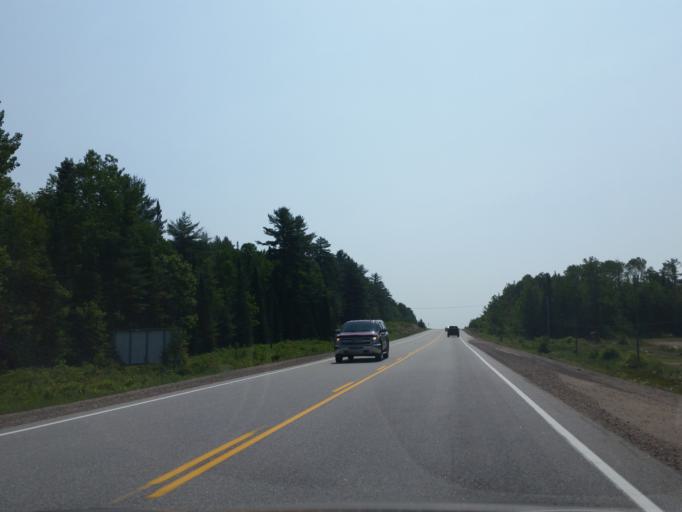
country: CA
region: Ontario
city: Mattawa
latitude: 46.3013
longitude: -78.5629
